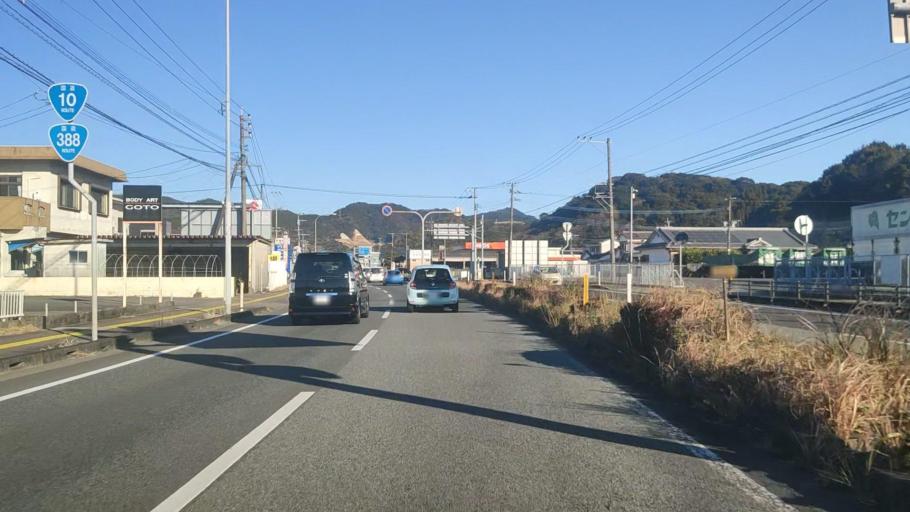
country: JP
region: Miyazaki
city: Nobeoka
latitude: 32.4889
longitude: 131.6643
